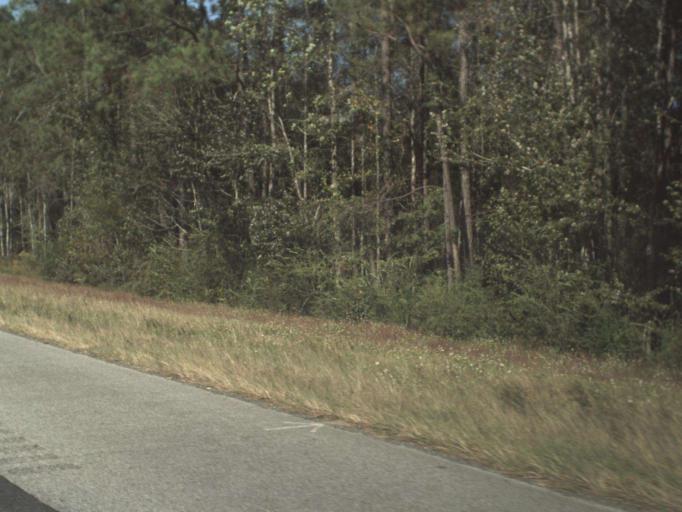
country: US
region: Florida
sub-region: Washington County
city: Chipley
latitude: 30.7529
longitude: -85.5903
